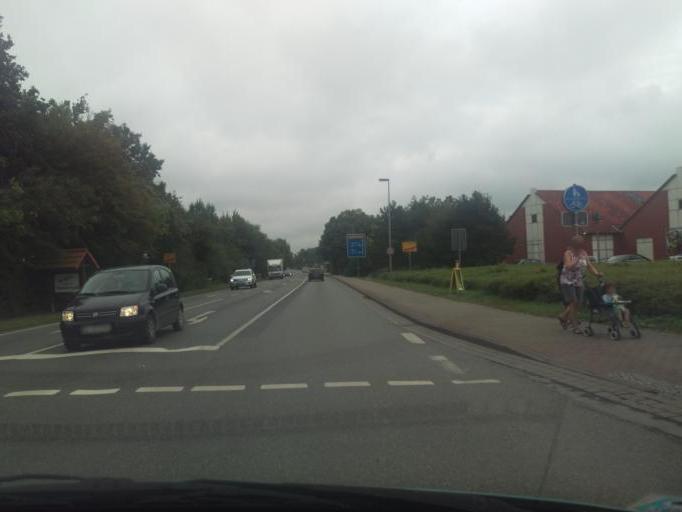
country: DE
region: Lower Saxony
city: Arpke
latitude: 52.3587
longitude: 10.1179
